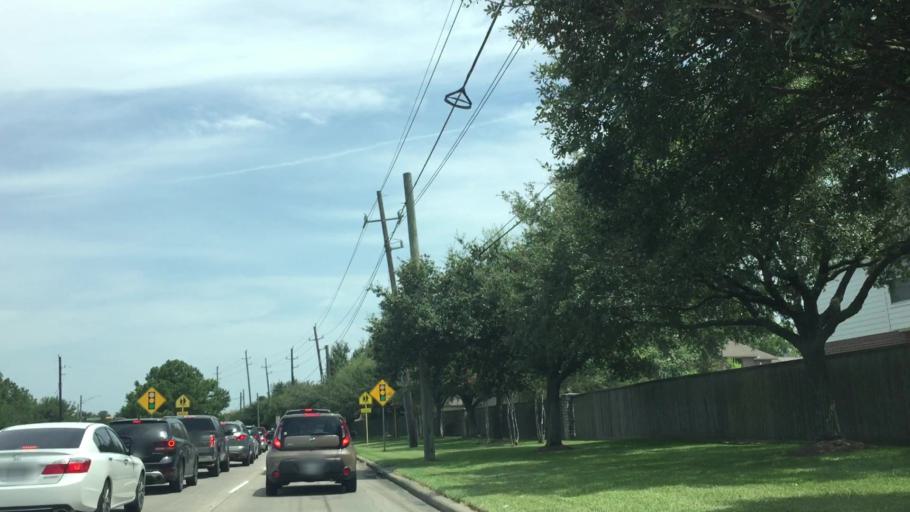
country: US
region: Texas
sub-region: Harris County
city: Jersey Village
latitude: 29.9048
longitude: -95.5595
